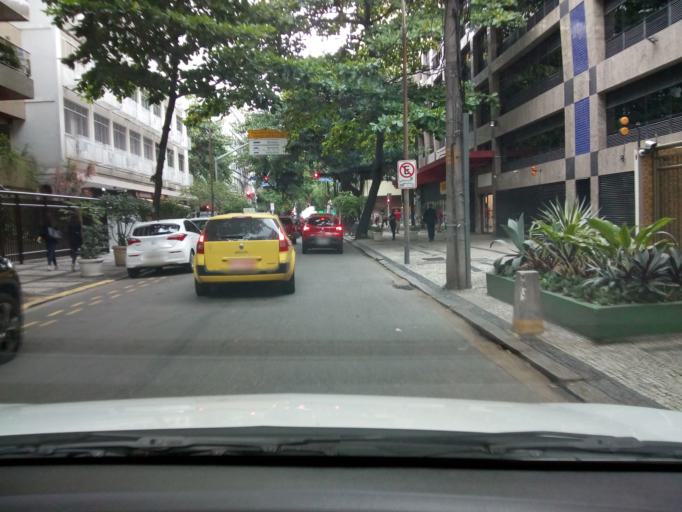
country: BR
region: Rio de Janeiro
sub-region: Rio De Janeiro
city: Rio de Janeiro
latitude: -22.9841
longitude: -43.2253
